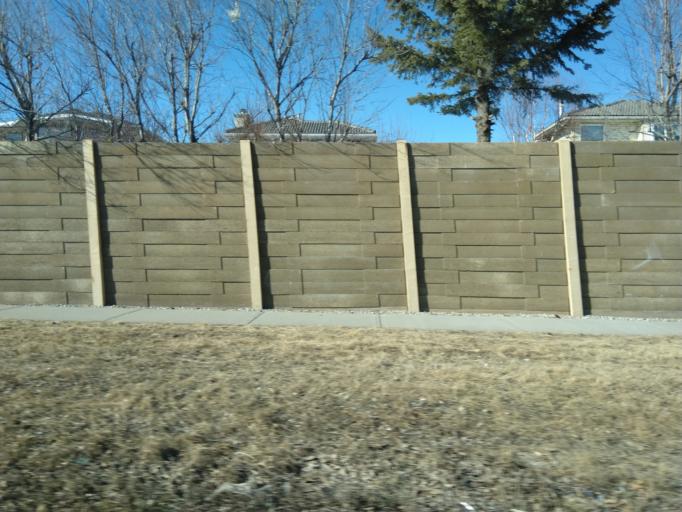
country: CA
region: Alberta
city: Calgary
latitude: 51.1389
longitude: -114.1559
